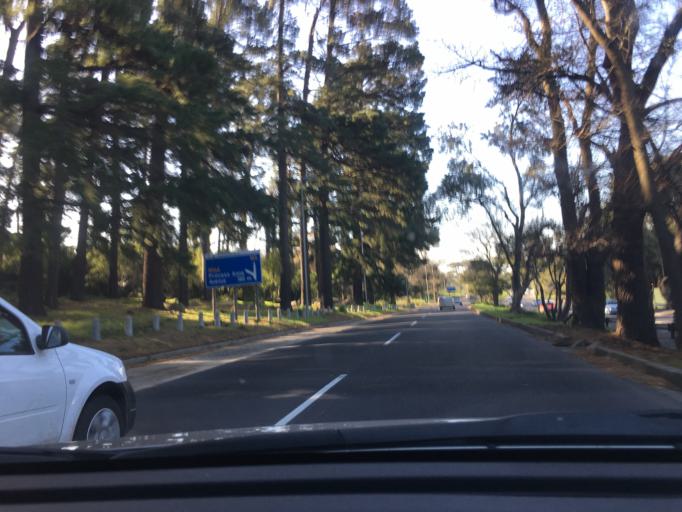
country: ZA
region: Western Cape
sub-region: City of Cape Town
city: Newlands
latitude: -33.9671
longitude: 18.4560
